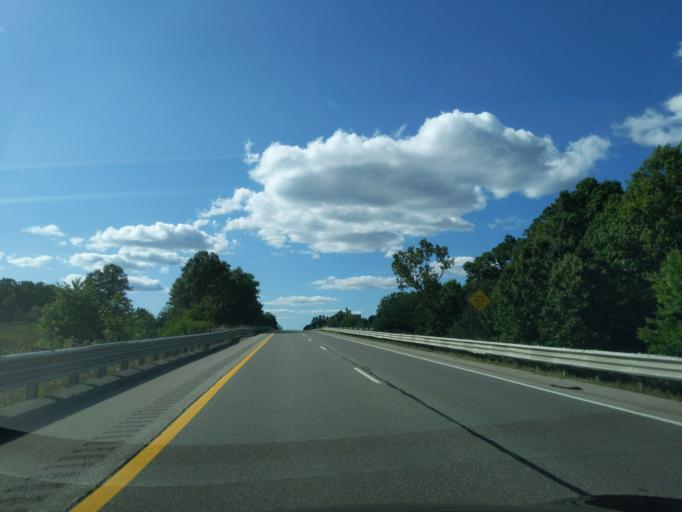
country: US
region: Michigan
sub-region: Muskegon County
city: Fruitport
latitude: 43.1370
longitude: -86.1525
